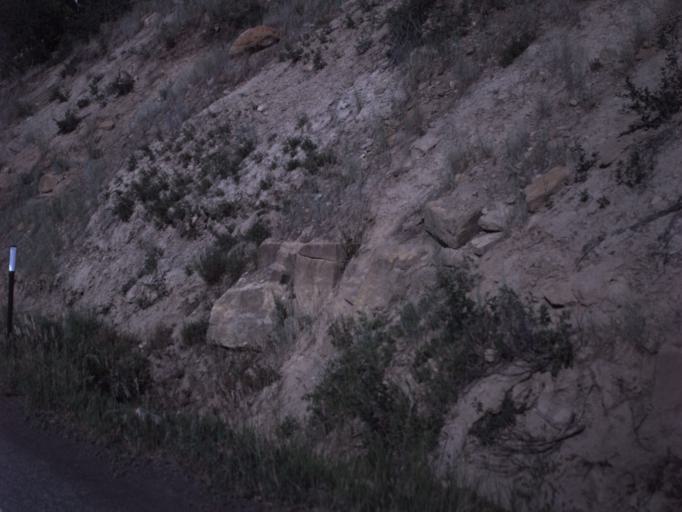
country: US
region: Utah
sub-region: Sanpete County
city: Fairview
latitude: 39.6608
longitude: -111.3494
